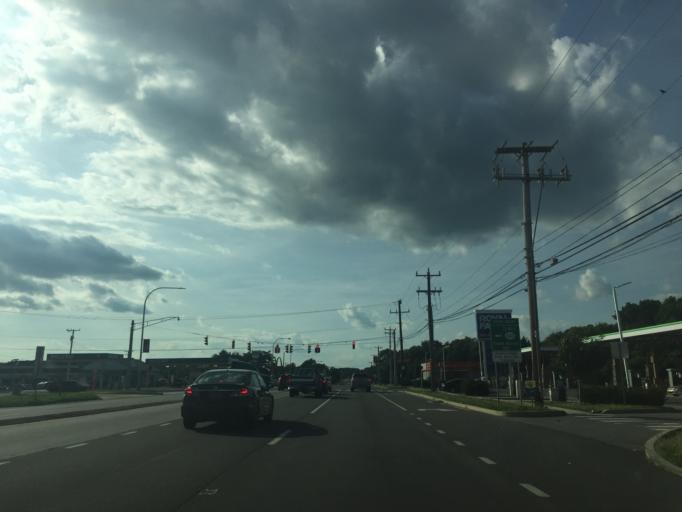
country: US
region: Delaware
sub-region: Kent County
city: Smyrna
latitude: 39.3055
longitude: -75.6062
